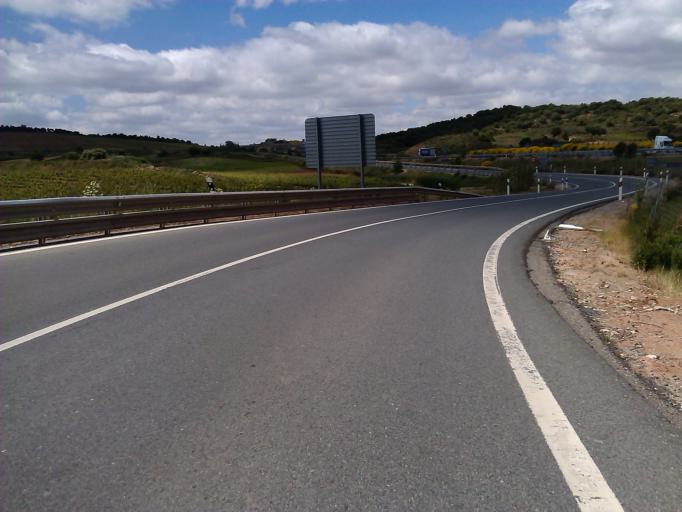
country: ES
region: La Rioja
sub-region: Provincia de La Rioja
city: Ventosa
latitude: 42.4125
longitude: -2.6290
